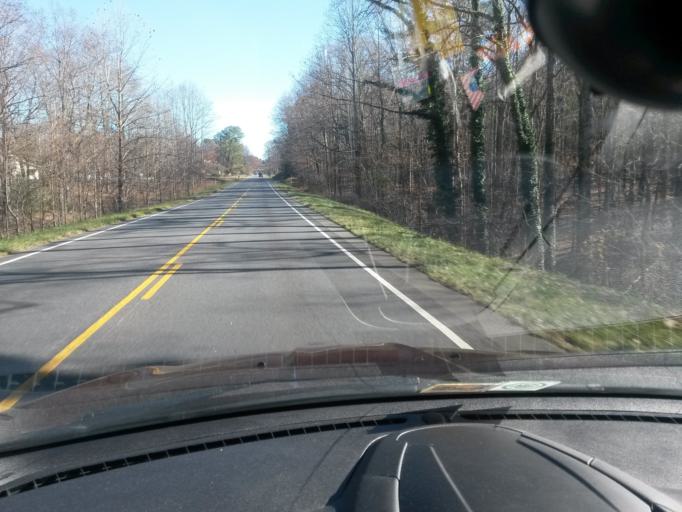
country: US
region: Virginia
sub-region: Henry County
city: Bassett
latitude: 36.7614
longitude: -80.0449
